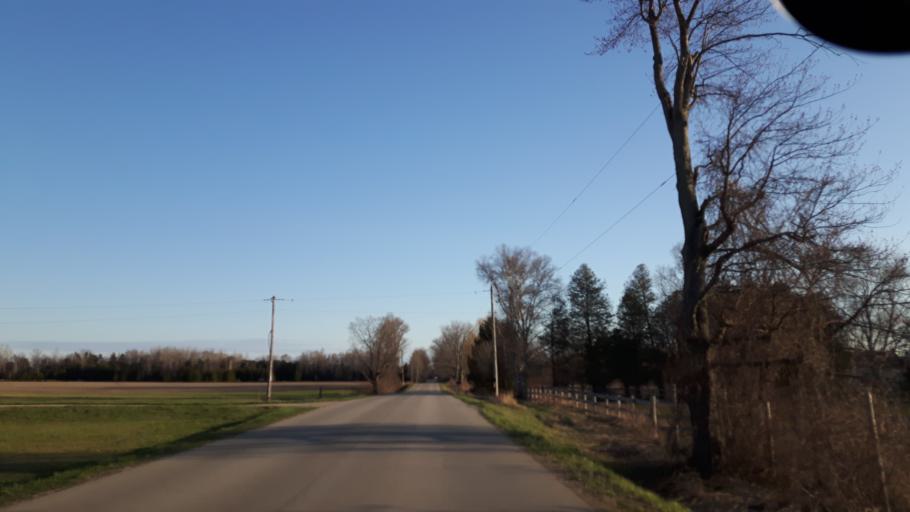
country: CA
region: Ontario
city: Goderich
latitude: 43.6305
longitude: -81.6847
